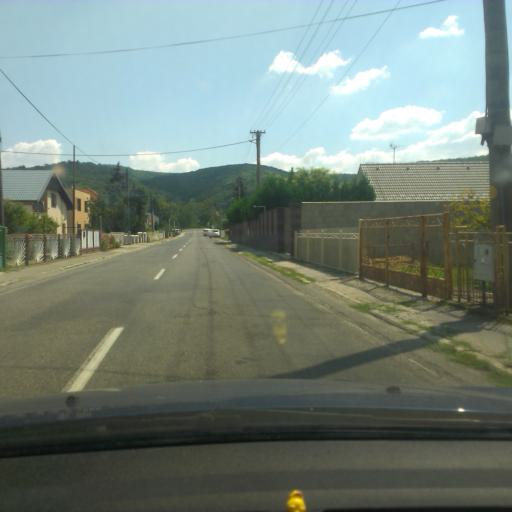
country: SK
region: Trnavsky
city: Hlohovec
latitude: 48.5098
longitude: 17.8261
